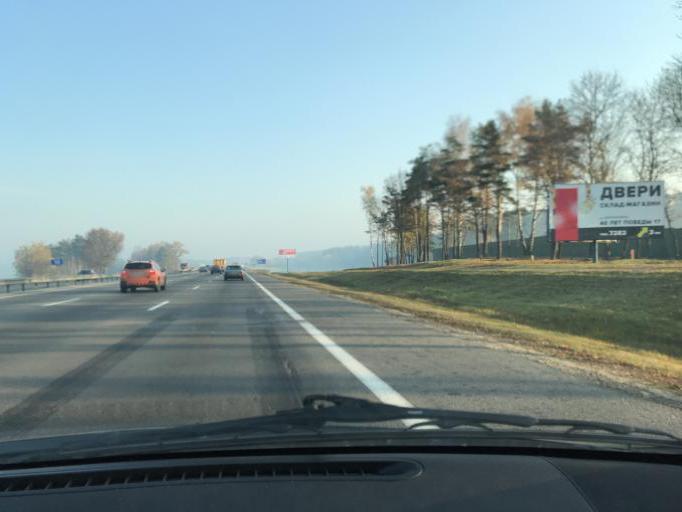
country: BY
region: Minsk
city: Borovlyany
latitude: 53.9718
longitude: 27.6482
